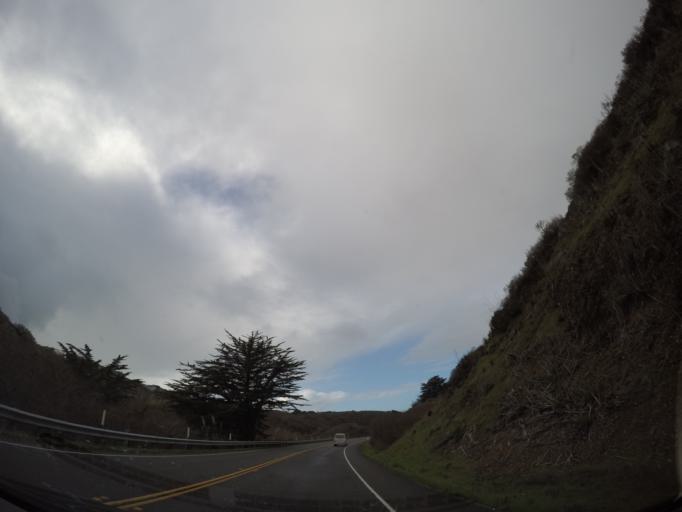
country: US
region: California
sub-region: Sonoma County
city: Bodega Bay
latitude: 38.3189
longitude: -123.0151
